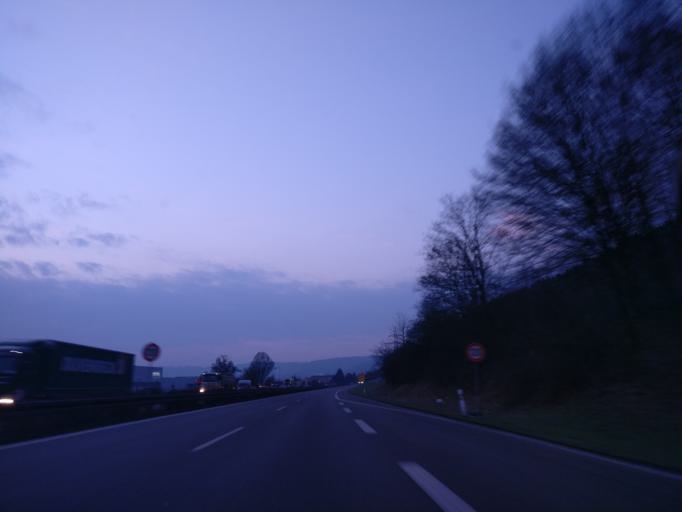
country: DE
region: Baden-Wuerttemberg
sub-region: Regierungsbezirk Stuttgart
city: Pluderhausen
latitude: 48.7998
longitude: 9.5793
